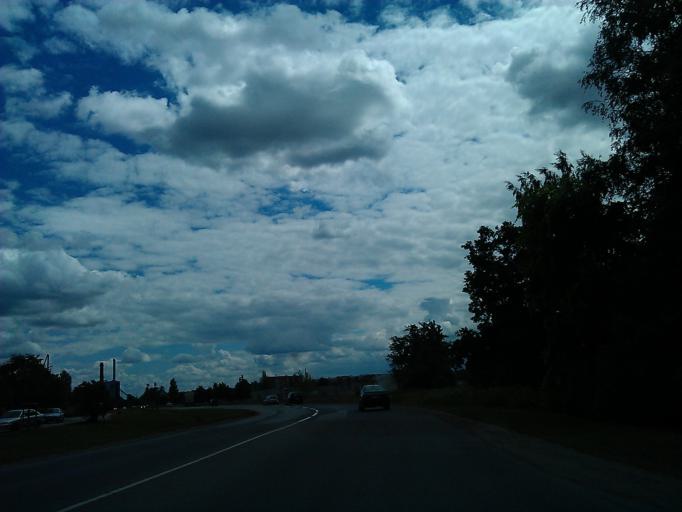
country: LV
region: Jelgava
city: Jelgava
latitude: 56.6407
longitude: 23.6972
